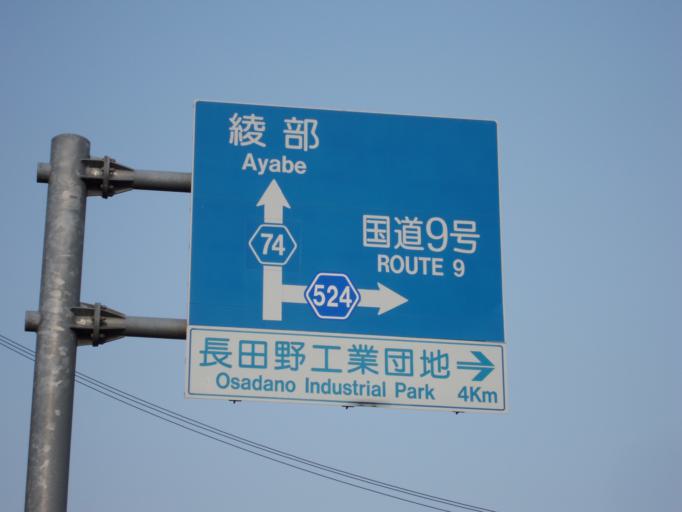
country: JP
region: Kyoto
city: Fukuchiyama
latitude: 35.3113
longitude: 135.1694
